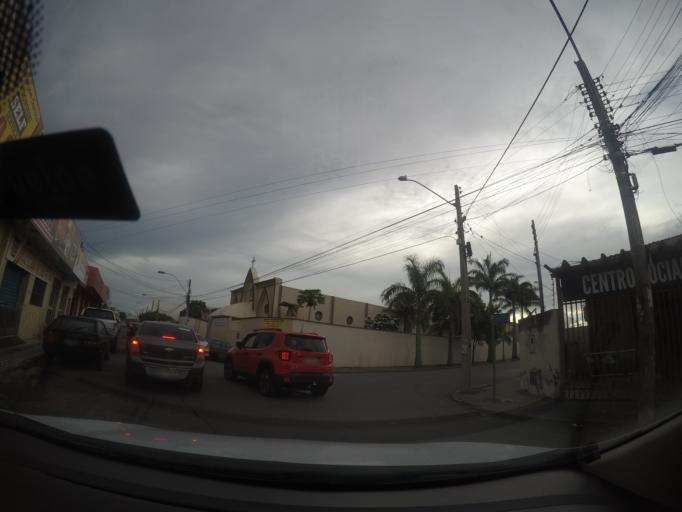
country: BR
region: Goias
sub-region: Goiania
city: Goiania
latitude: -16.6740
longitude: -49.2916
